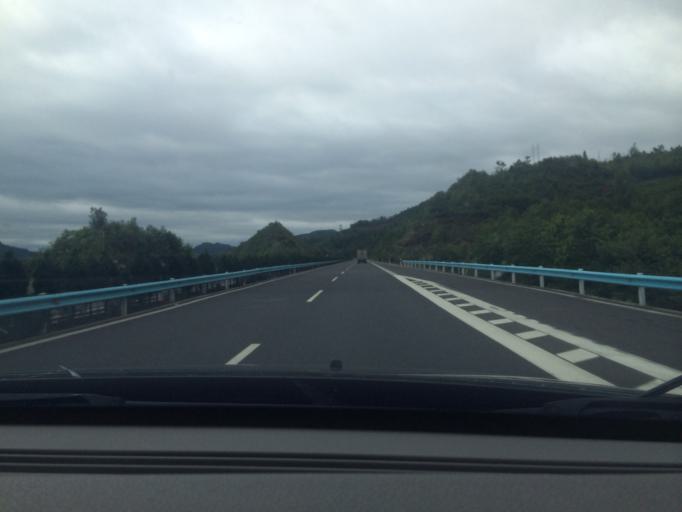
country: CN
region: Guangxi Zhuangzu Zizhiqu
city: Xinzhou
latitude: 25.5387
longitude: 105.1440
